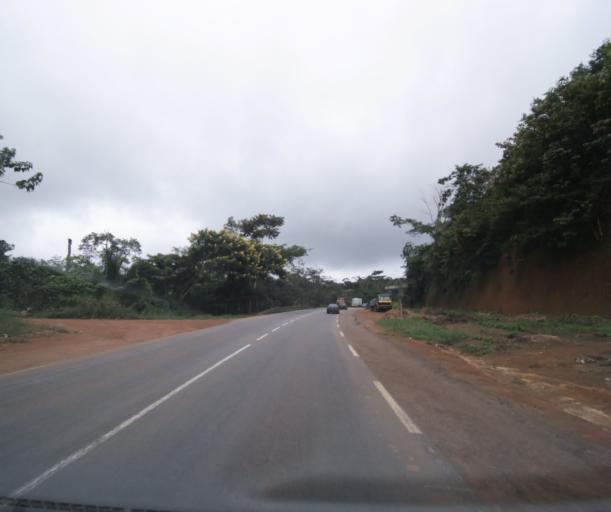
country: CM
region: Centre
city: Mbankomo
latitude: 3.7808
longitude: 11.2655
